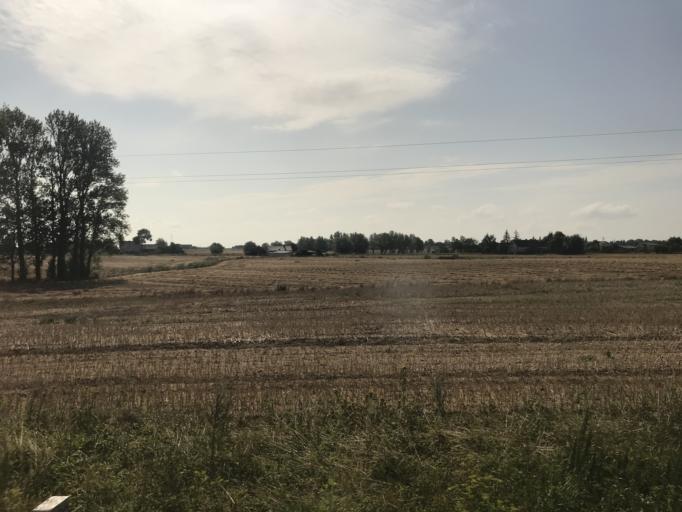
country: PL
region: Kujawsko-Pomorskie
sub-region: Powiat swiecki
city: Pruszcz
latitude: 53.3517
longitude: 18.2263
